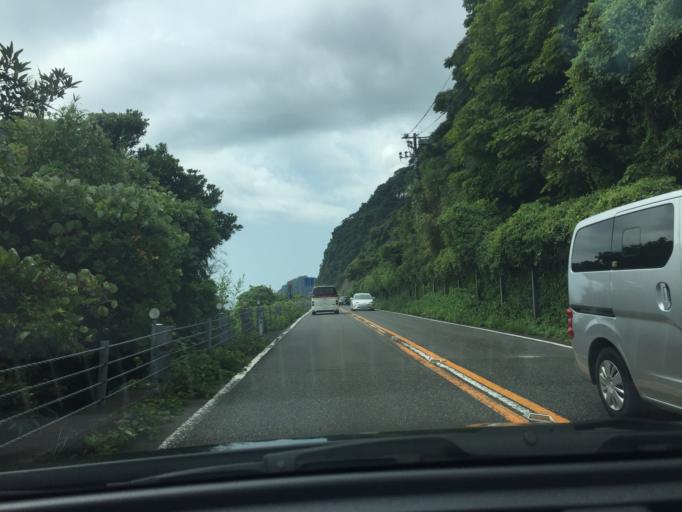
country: JP
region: Shizuoka
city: Ito
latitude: 34.8525
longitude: 139.0822
